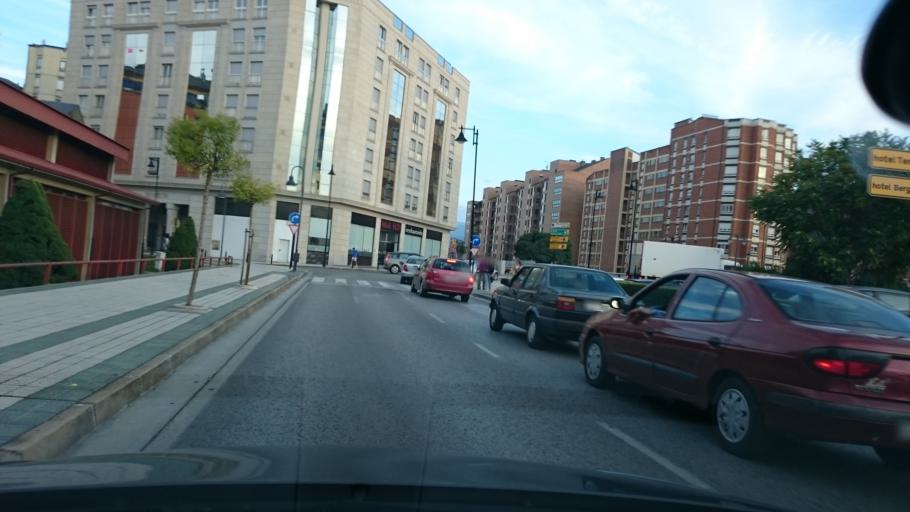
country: ES
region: Castille and Leon
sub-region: Provincia de Leon
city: Ponferrada
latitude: 42.5478
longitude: -6.6047
